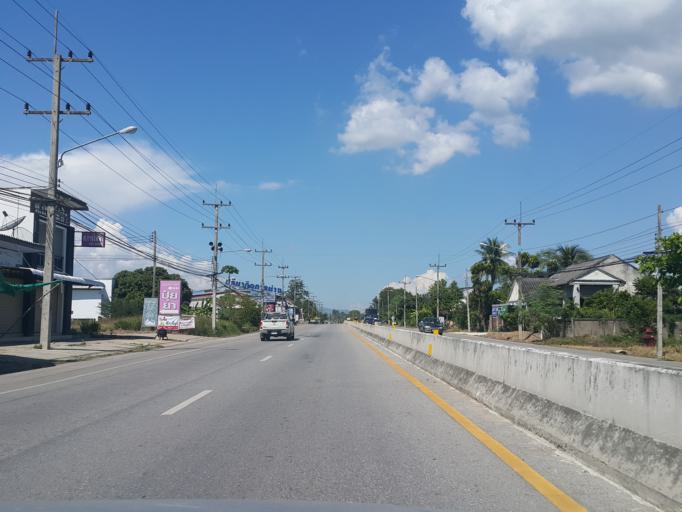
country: TH
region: Chiang Mai
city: Mae Taeng
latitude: 19.0387
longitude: 98.9466
